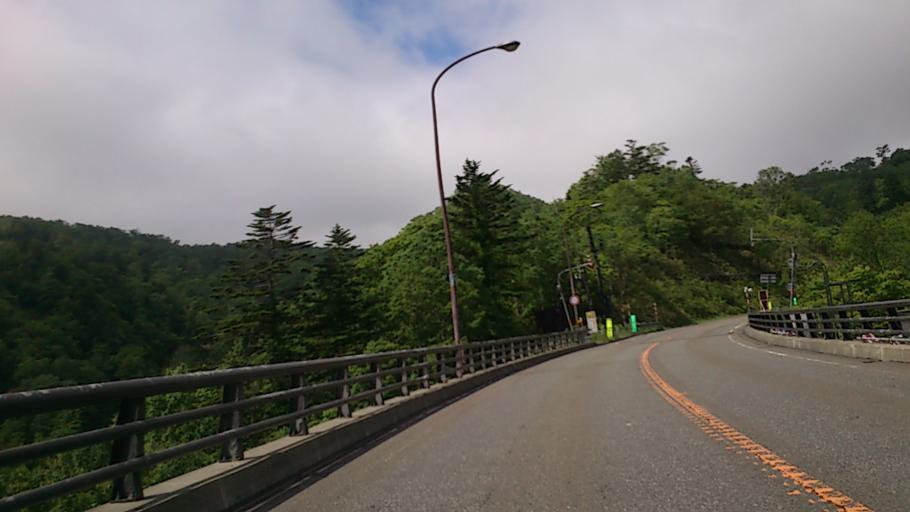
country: JP
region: Hokkaido
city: Shiraoi
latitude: 42.7096
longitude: 141.1962
